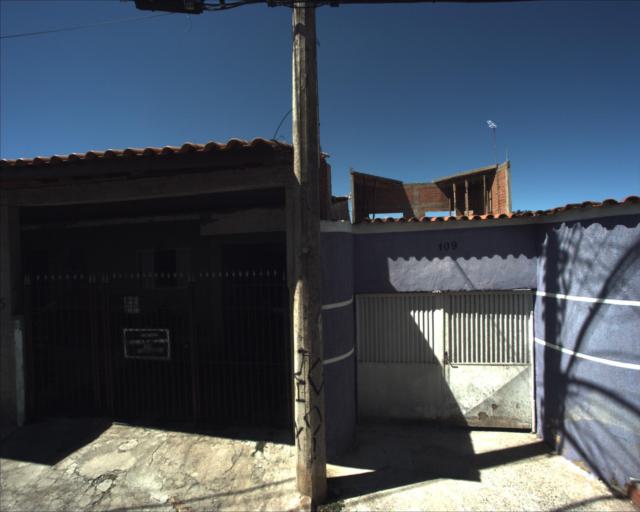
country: BR
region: Sao Paulo
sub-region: Votorantim
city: Votorantim
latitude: -23.5161
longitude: -47.4267
